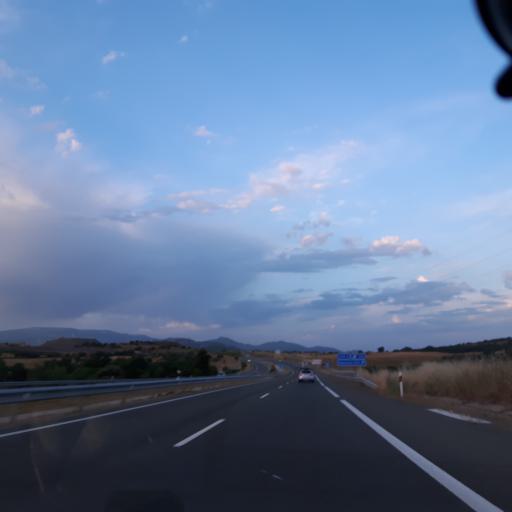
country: ES
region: Castille and Leon
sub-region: Provincia de Salamanca
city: Guijuelo
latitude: 40.5316
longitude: -5.6677
